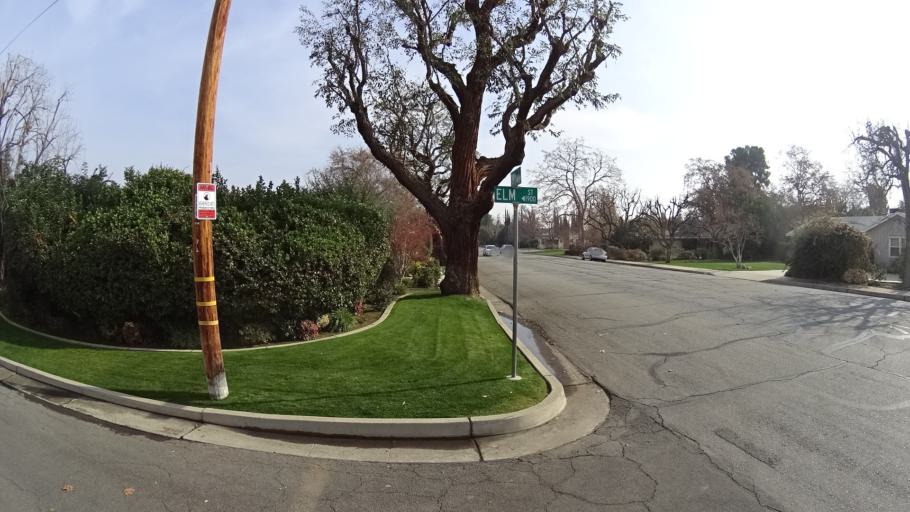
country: US
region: California
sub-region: Kern County
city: Bakersfield
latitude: 35.3763
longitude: -119.0363
